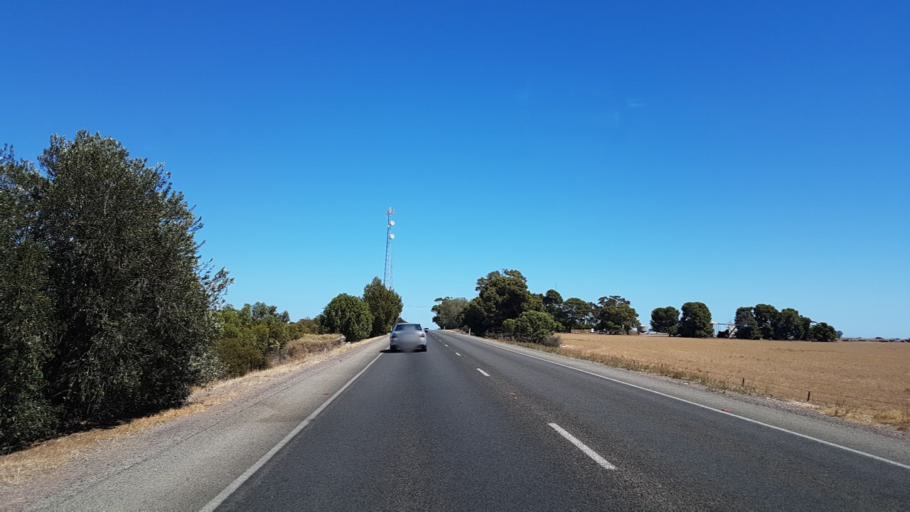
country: AU
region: South Australia
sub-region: Copper Coast
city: Wallaroo
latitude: -33.9496
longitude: 137.6737
